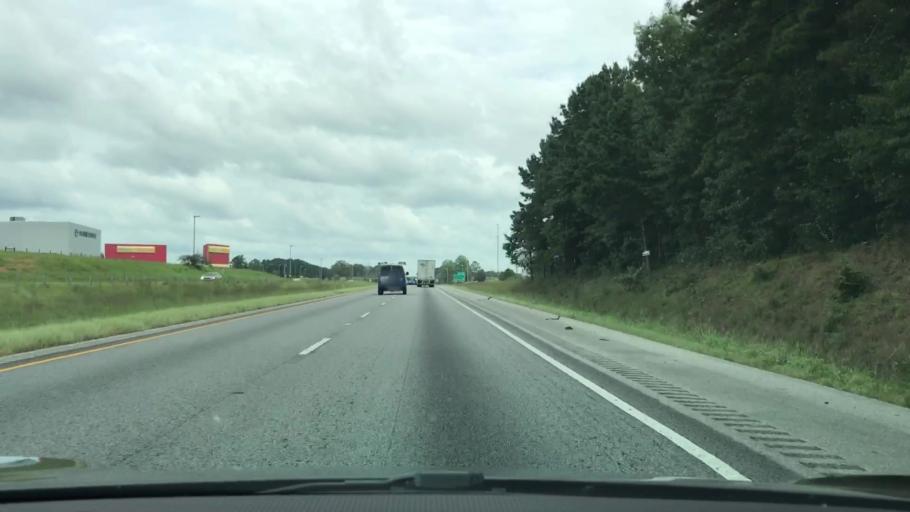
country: US
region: Alabama
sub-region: Chambers County
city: Huguley
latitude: 32.7403
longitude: -85.2856
